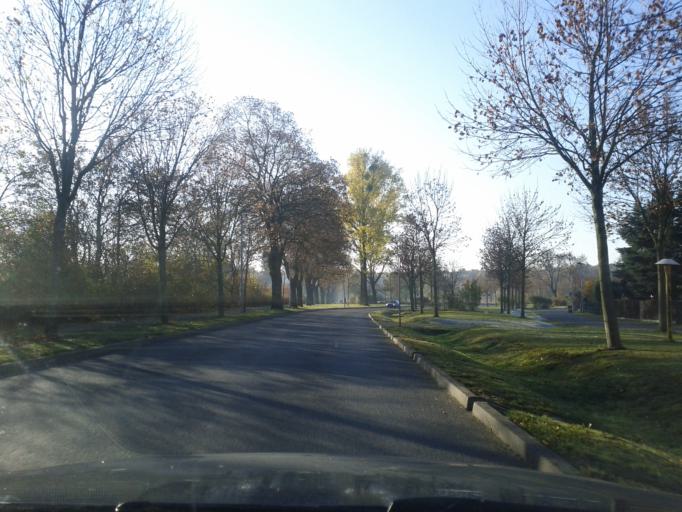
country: DE
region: Brandenburg
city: Schoneiche
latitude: 52.4696
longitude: 13.7310
